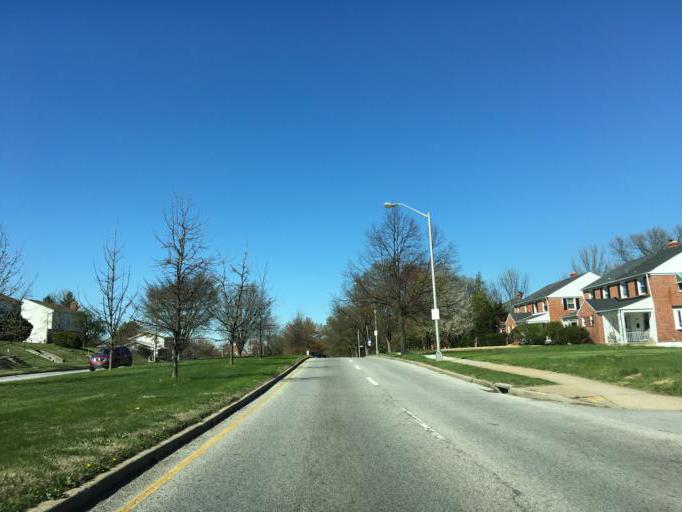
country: US
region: Maryland
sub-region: Baltimore County
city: Towson
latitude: 39.3615
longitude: -76.5877
